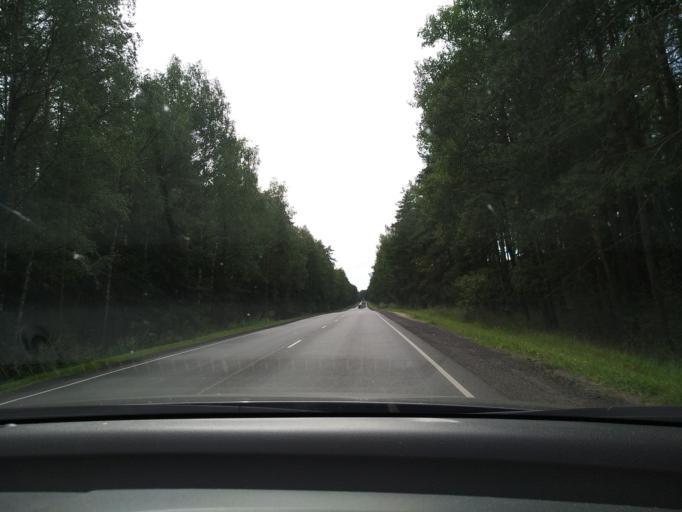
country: RU
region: Moskovskaya
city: Krasnyy Tkach
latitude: 55.3981
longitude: 39.1231
